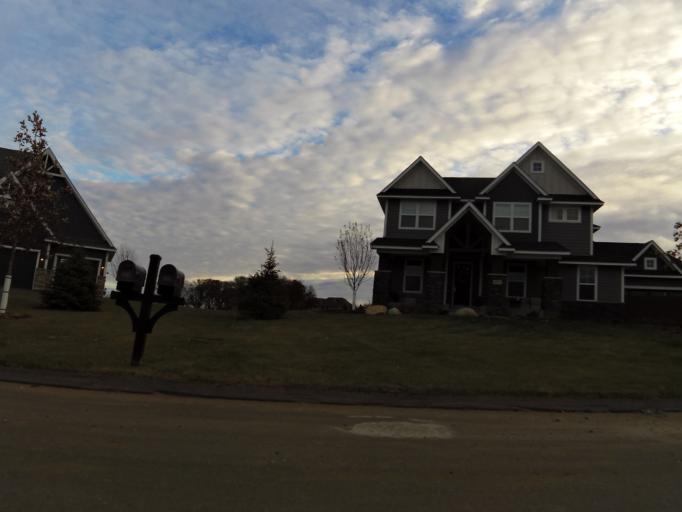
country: US
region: Minnesota
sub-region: Washington County
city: Bayport
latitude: 45.0016
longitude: -92.7957
